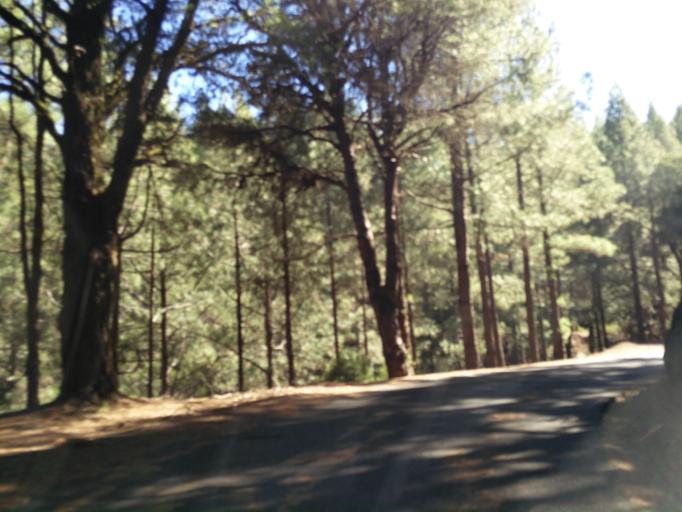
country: ES
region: Canary Islands
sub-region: Provincia de Santa Cruz de Tenerife
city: Brena Baja
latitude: 28.6137
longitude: -17.8411
